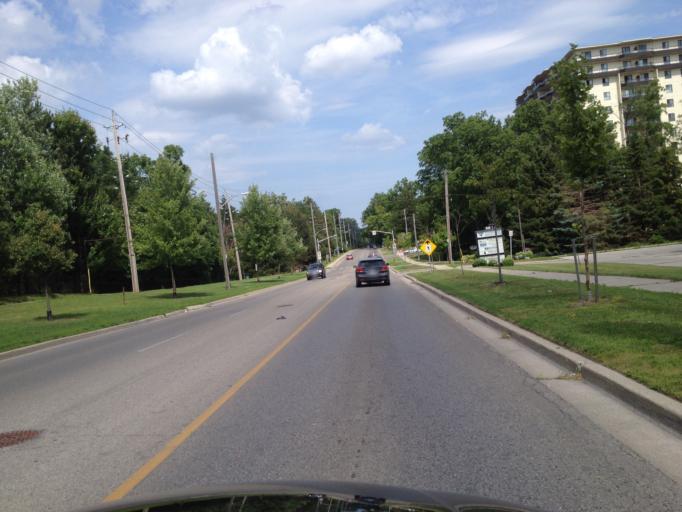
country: CA
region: Ontario
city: London
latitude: 43.0207
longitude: -81.2574
